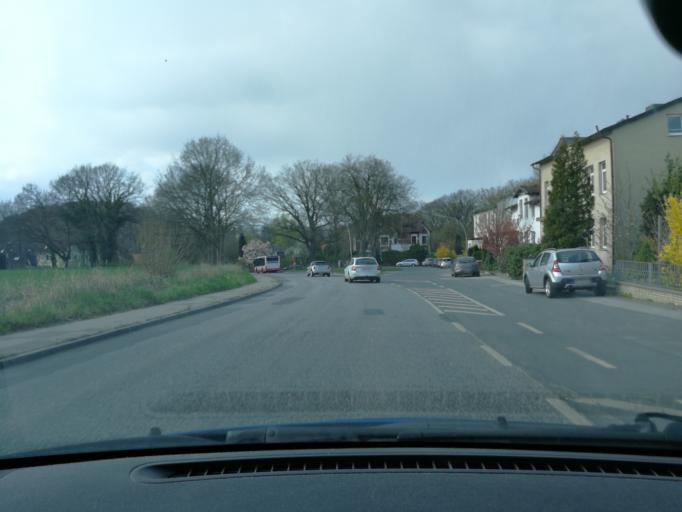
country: DE
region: Hamburg
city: Harburg
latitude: 53.4333
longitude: 10.0119
